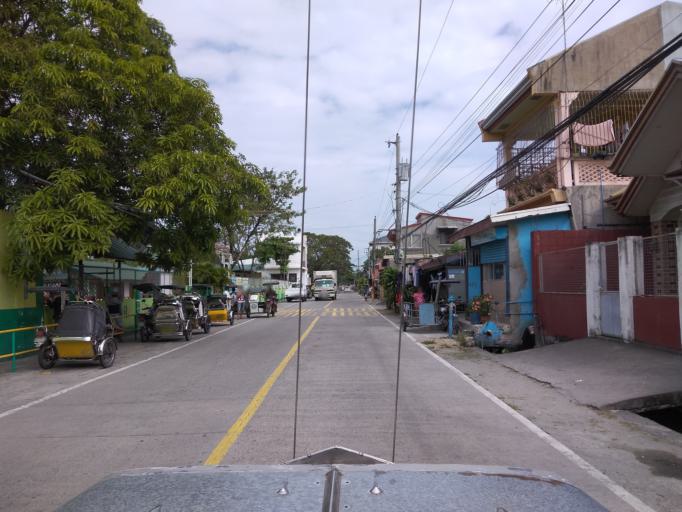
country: PH
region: Central Luzon
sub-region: Province of Pampanga
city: Sexmoan
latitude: 14.9480
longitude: 120.6235
